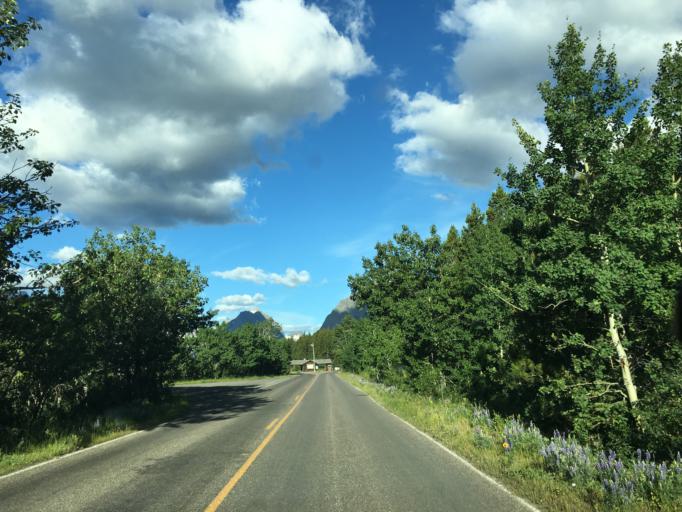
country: CA
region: Alberta
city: Cardston
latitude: 48.8229
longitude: -113.5767
